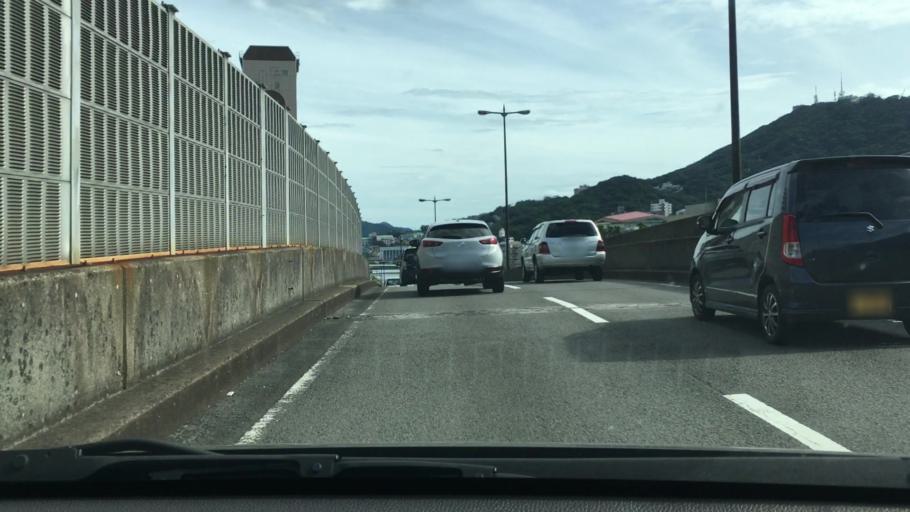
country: JP
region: Nagasaki
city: Nagasaki-shi
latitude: 32.7702
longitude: 129.8625
